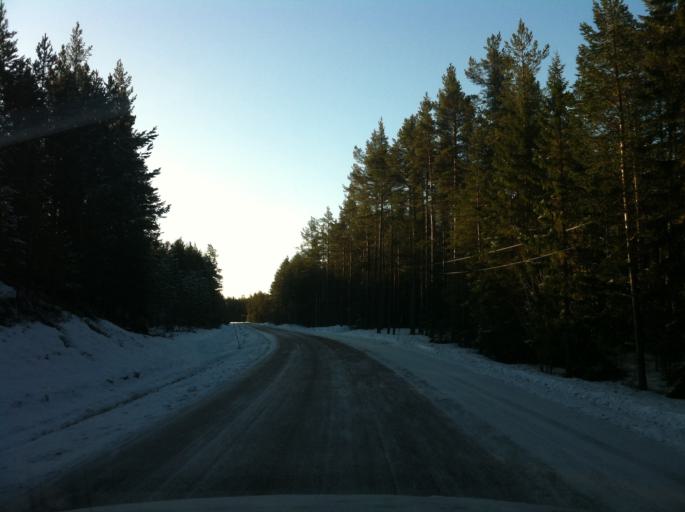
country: SE
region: Dalarna
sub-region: Orsa Kommun
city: Orsa
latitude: 61.1598
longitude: 14.5146
